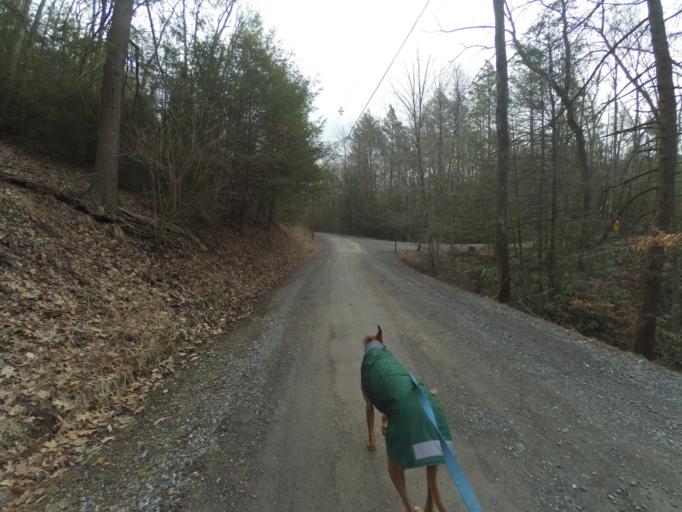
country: US
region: Pennsylvania
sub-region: Centre County
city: Boalsburg
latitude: 40.7603
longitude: -77.7093
